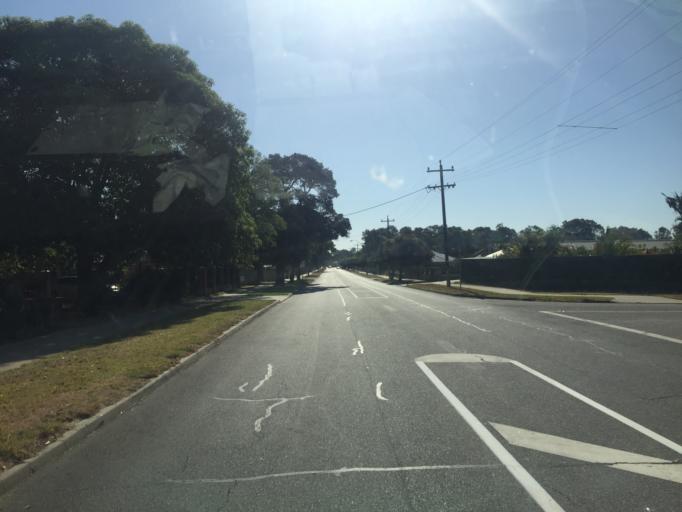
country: AU
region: Western Australia
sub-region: Gosnells
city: Kenwick
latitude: -32.0349
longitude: 115.9755
